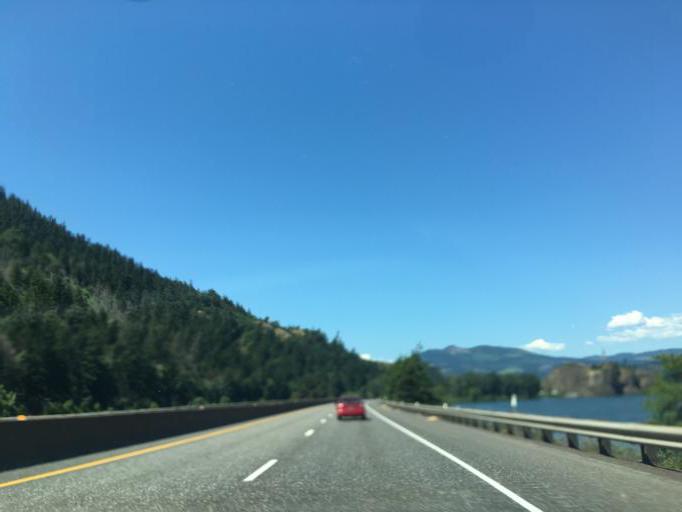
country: US
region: Washington
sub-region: Klickitat County
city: White Salmon
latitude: 45.6985
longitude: -121.4654
